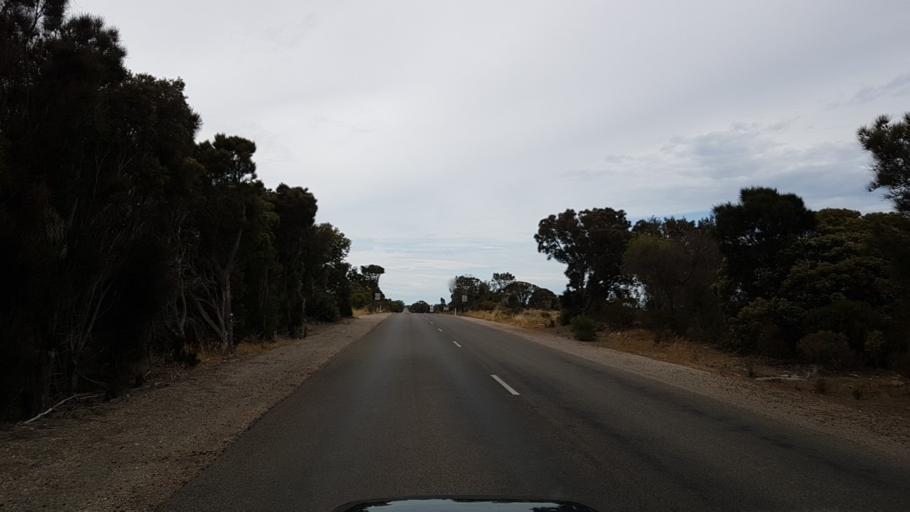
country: AU
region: South Australia
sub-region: Yorke Peninsula
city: Port Victoria
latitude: -34.9278
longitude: 137.0851
